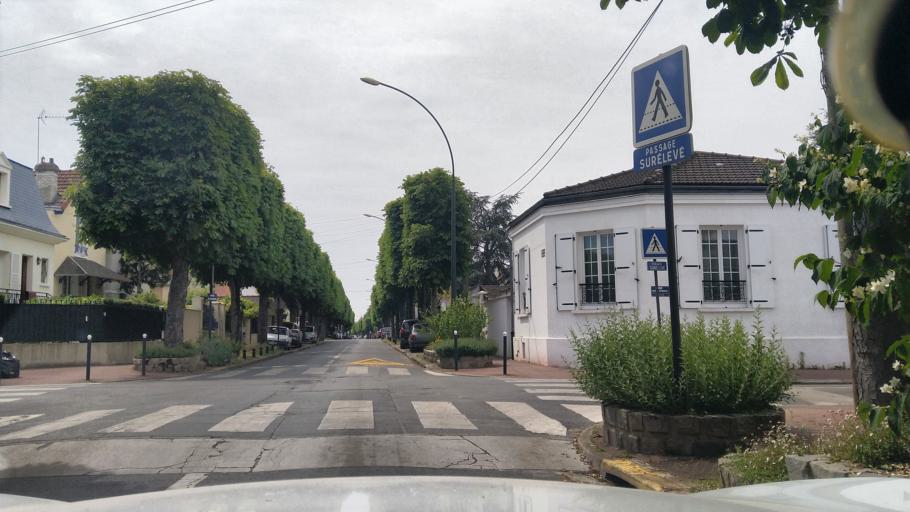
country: FR
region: Ile-de-France
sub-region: Departement du Val-de-Marne
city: Saint-Maur-des-Fosses
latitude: 48.7986
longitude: 2.5084
